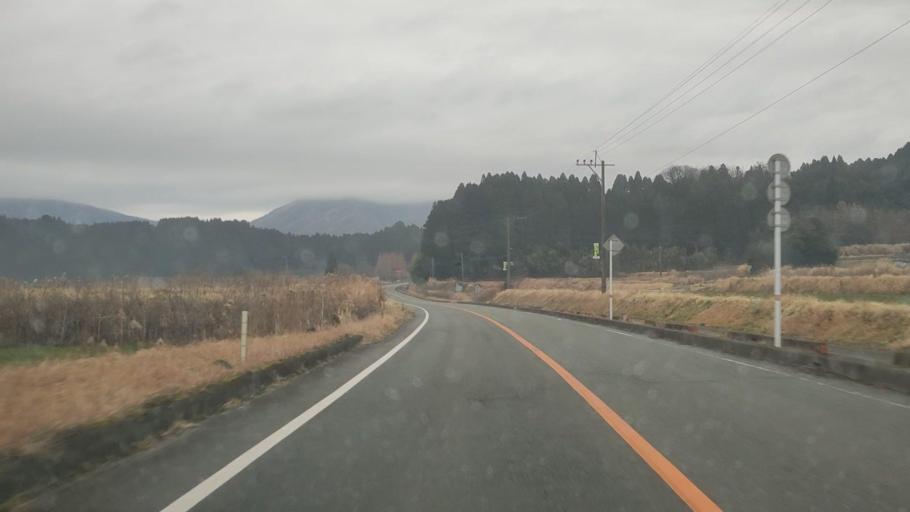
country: JP
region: Kumamoto
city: Aso
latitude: 32.8290
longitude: 131.1331
